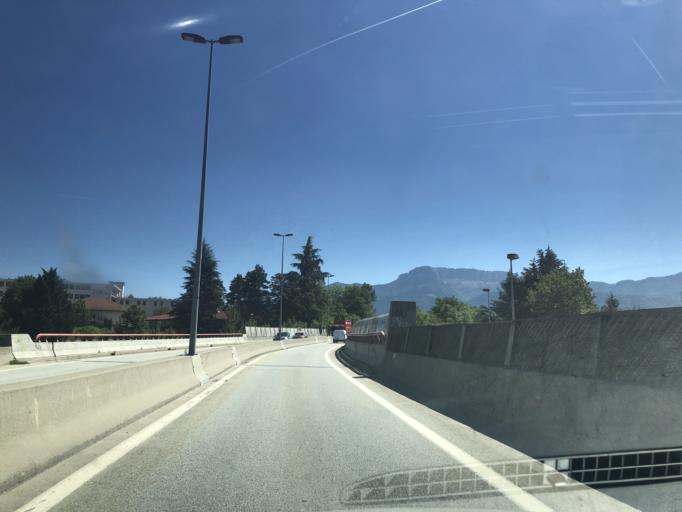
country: FR
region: Rhone-Alpes
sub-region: Departement de la Haute-Savoie
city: Pringy
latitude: 45.9350
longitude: 6.1228
